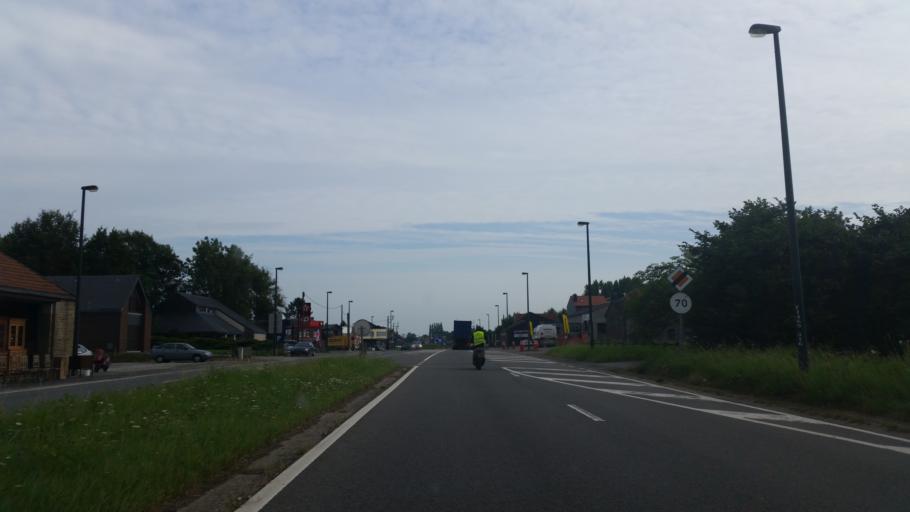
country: BE
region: Wallonia
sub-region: Province de Liege
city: Nandrin
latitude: 50.5047
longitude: 5.3958
